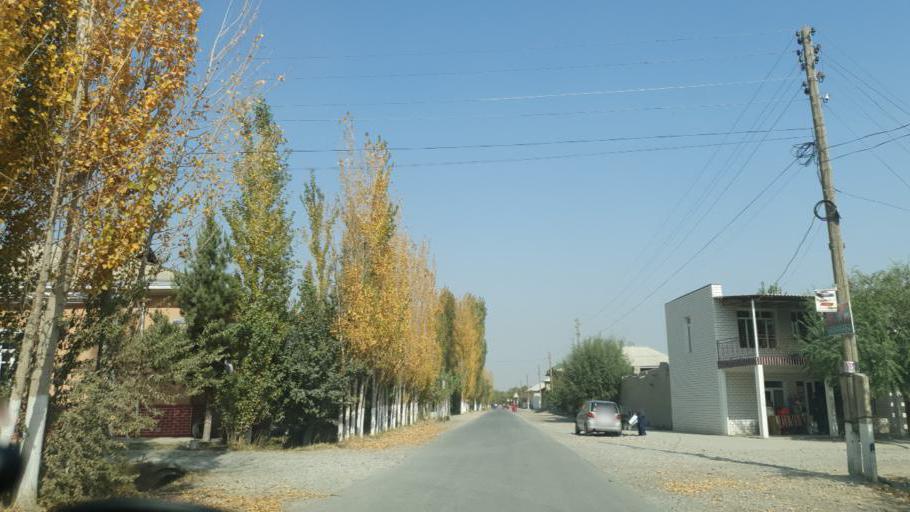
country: UZ
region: Fergana
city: Beshariq
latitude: 40.4920
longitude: 70.6210
